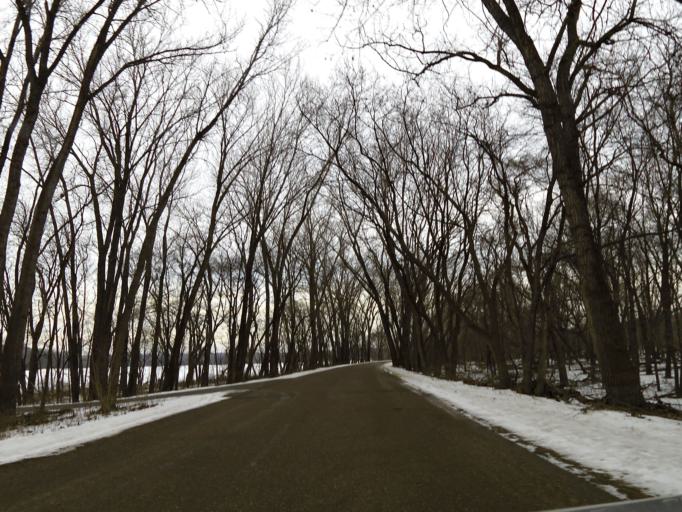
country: US
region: Minnesota
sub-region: Dakota County
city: Mendota Heights
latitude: 44.8751
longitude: -93.1904
